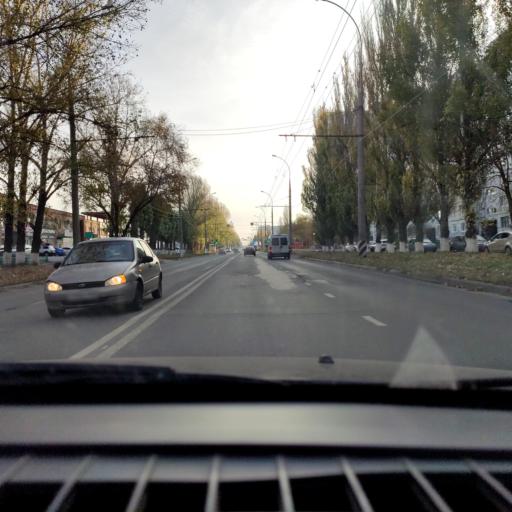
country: RU
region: Samara
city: Tol'yatti
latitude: 53.5367
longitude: 49.2932
